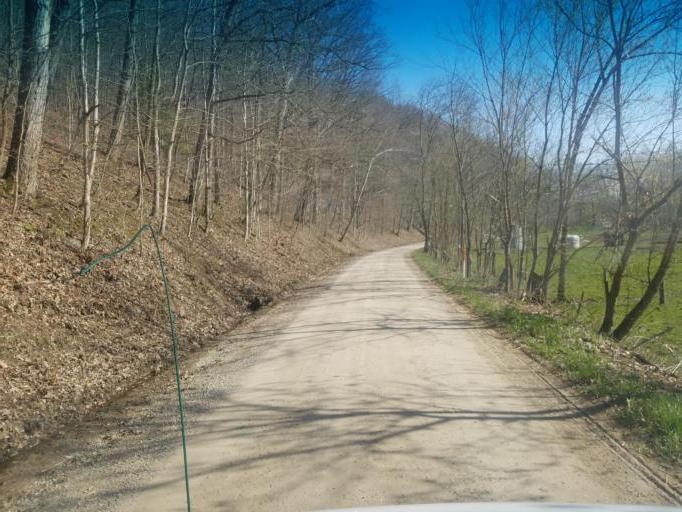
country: US
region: Ohio
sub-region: Muskingum County
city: Frazeysburg
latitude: 40.2236
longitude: -82.1798
